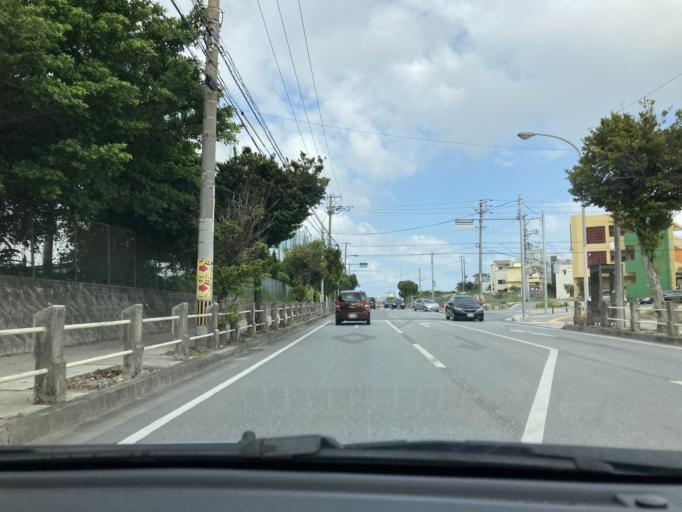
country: JP
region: Okinawa
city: Naha-shi
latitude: 26.2217
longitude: 127.7306
